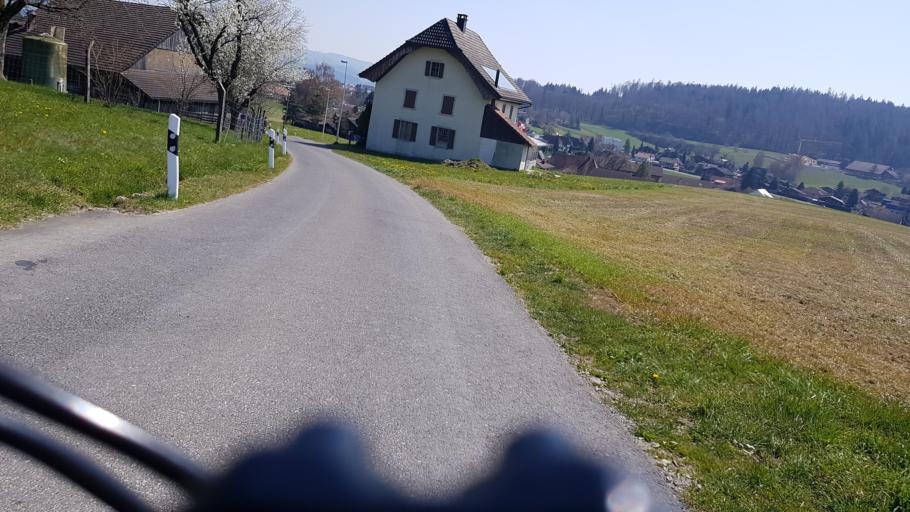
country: CH
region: Aargau
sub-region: Bezirk Kulm
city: Reinach
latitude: 47.2667
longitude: 8.1893
